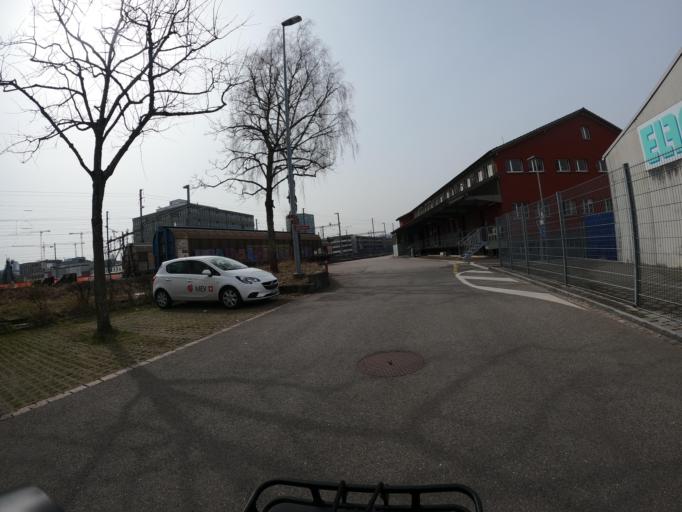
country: CH
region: Aargau
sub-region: Bezirk Aarau
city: Aarau
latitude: 47.3941
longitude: 8.0614
